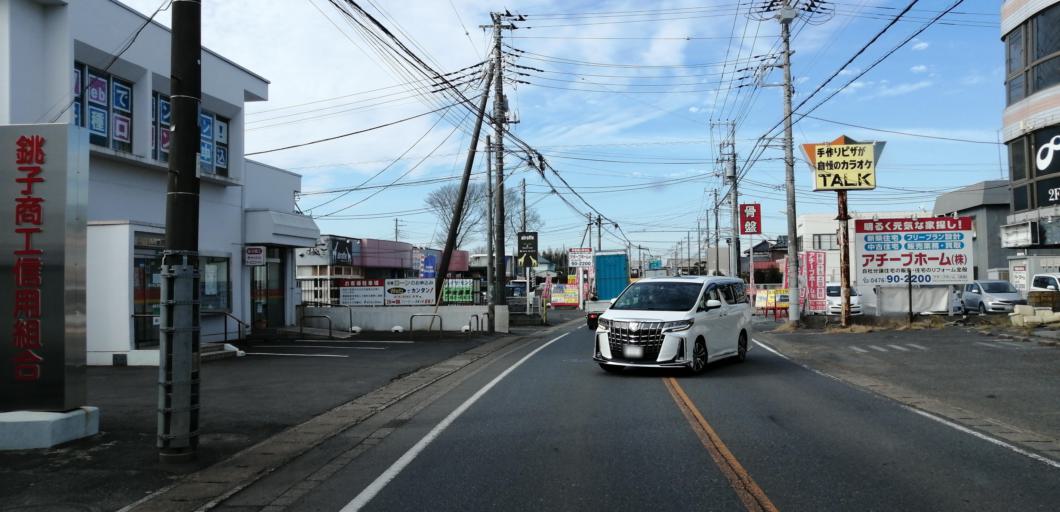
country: JP
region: Chiba
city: Narita
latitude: 35.7368
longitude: 140.3239
